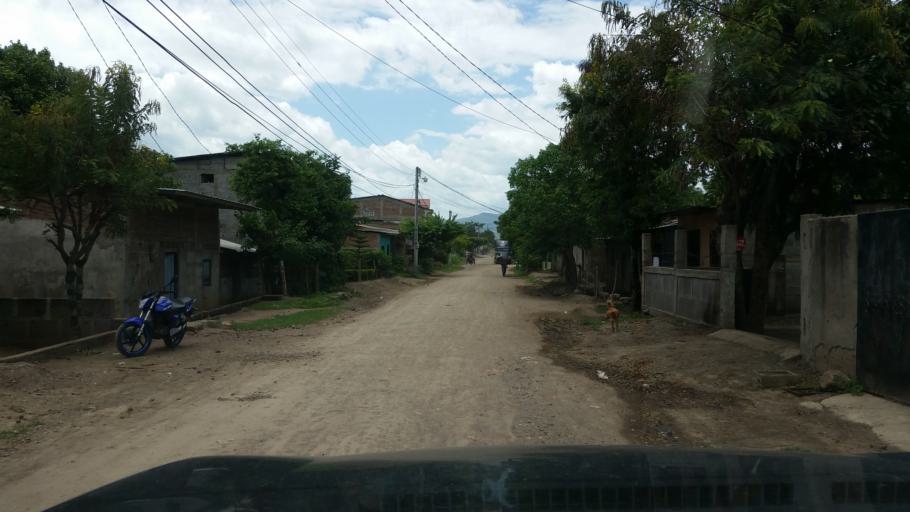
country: NI
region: Matagalpa
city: Ciudad Dario
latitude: 12.8599
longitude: -86.0914
